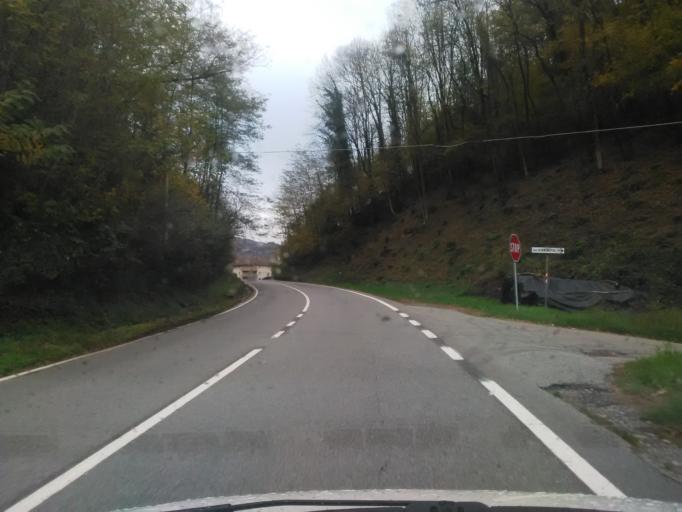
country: IT
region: Piedmont
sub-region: Provincia di Vercelli
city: Borgosesia
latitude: 45.7174
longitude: 8.3006
